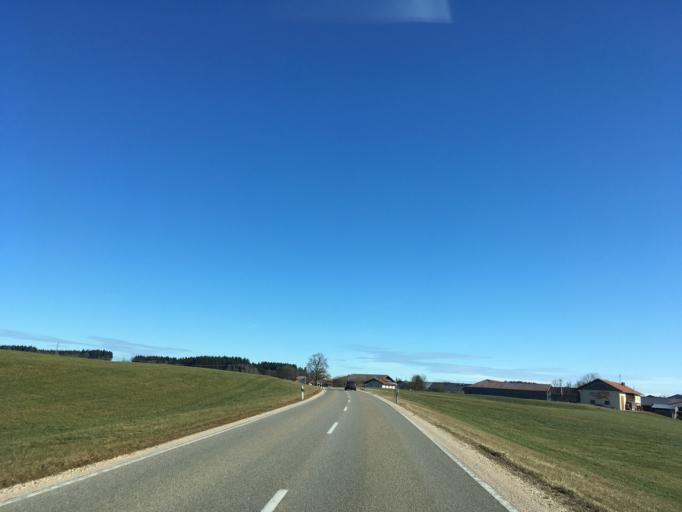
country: DE
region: Bavaria
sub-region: Upper Bavaria
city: Pittenhart
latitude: 47.9903
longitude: 12.3622
